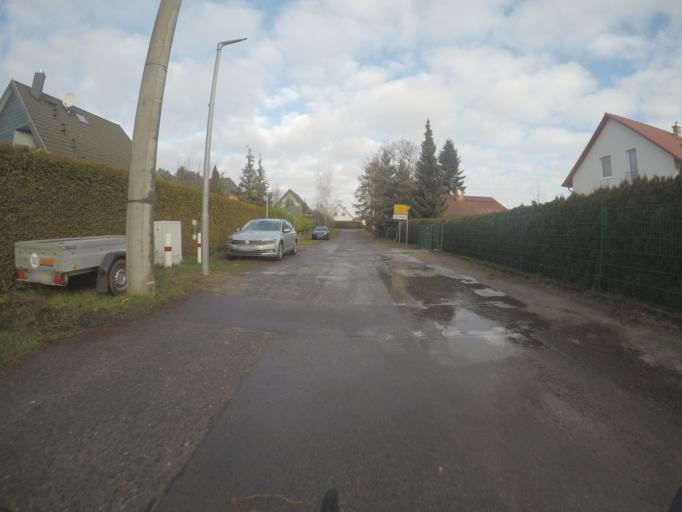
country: DE
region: Berlin
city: Falkenberg
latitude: 52.5896
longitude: 13.5383
